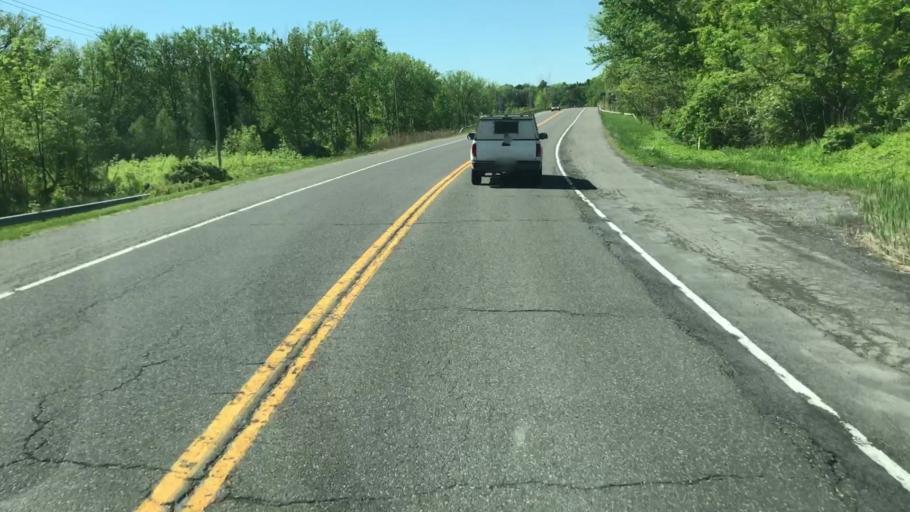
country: US
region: New York
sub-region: Onondaga County
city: Seneca Knolls
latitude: 43.1267
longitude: -76.2506
